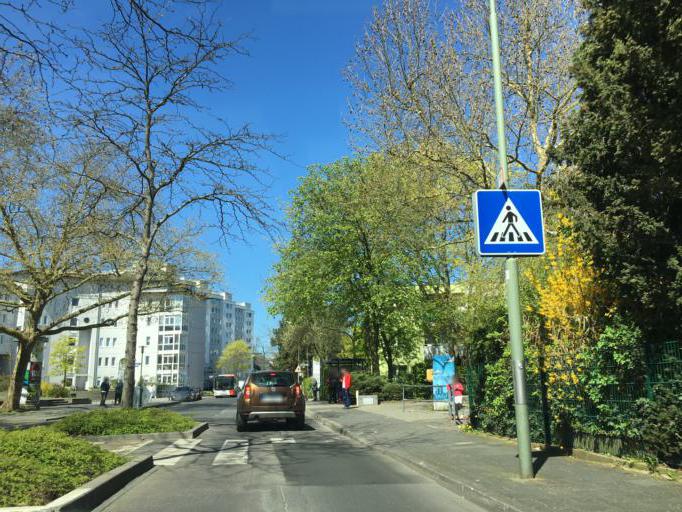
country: DE
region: Hesse
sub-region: Regierungsbezirk Darmstadt
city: Offenbach
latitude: 50.0855
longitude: 8.7544
